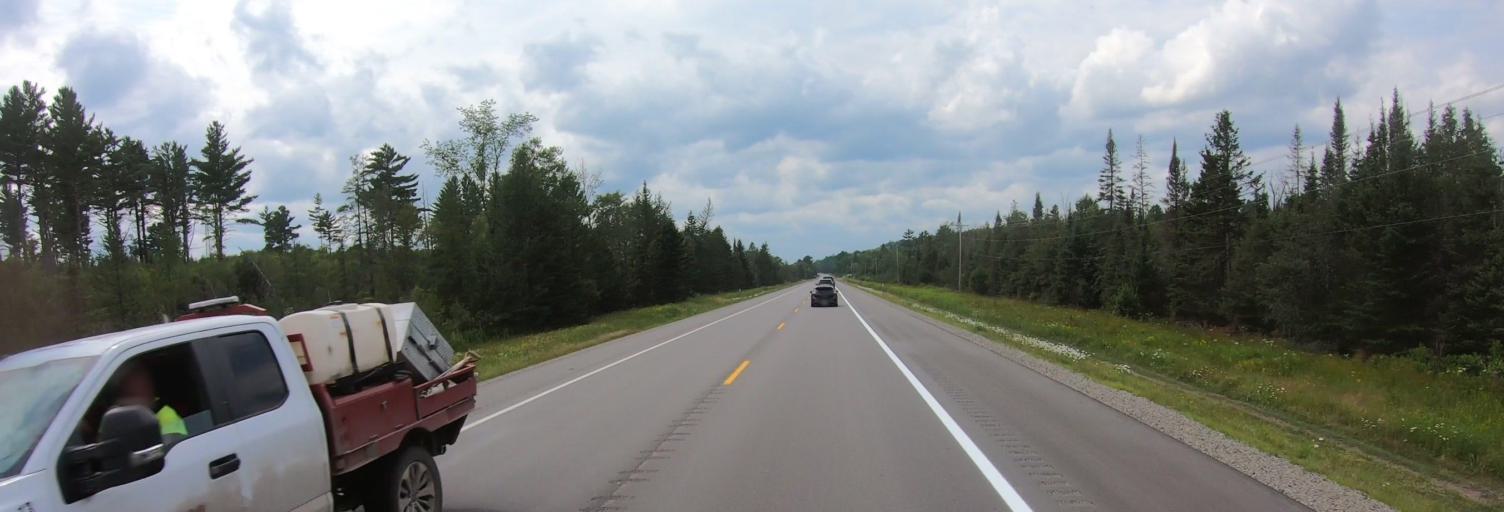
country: US
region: Michigan
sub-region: Baraga County
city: L'Anse
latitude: 46.5381
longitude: -88.1225
